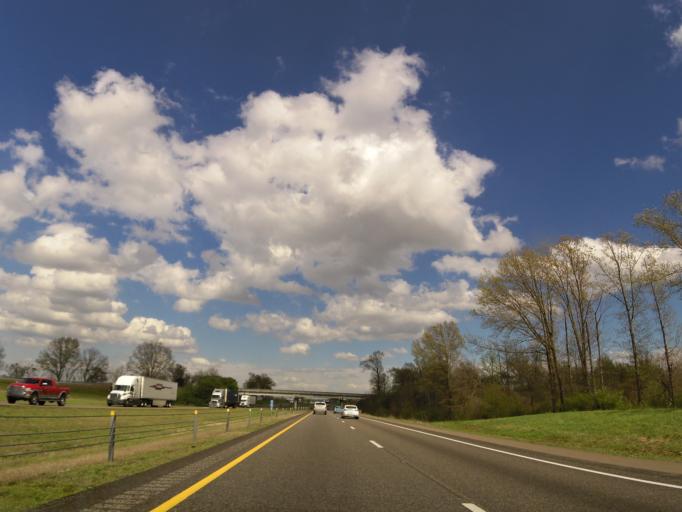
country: US
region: Tennessee
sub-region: Madison County
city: Jackson
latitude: 35.6322
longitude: -88.9517
